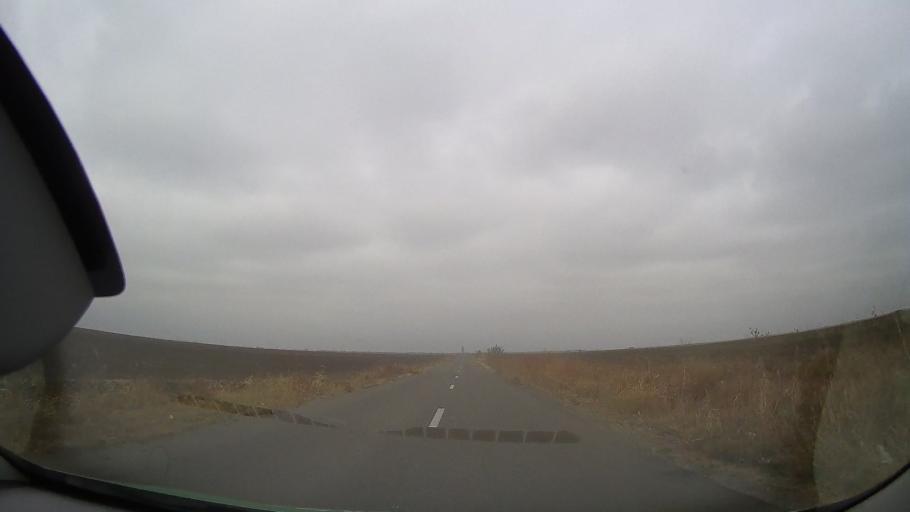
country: RO
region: Buzau
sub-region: Comuna Bradeanu
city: Bradeanu
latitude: 44.8925
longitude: 26.8739
